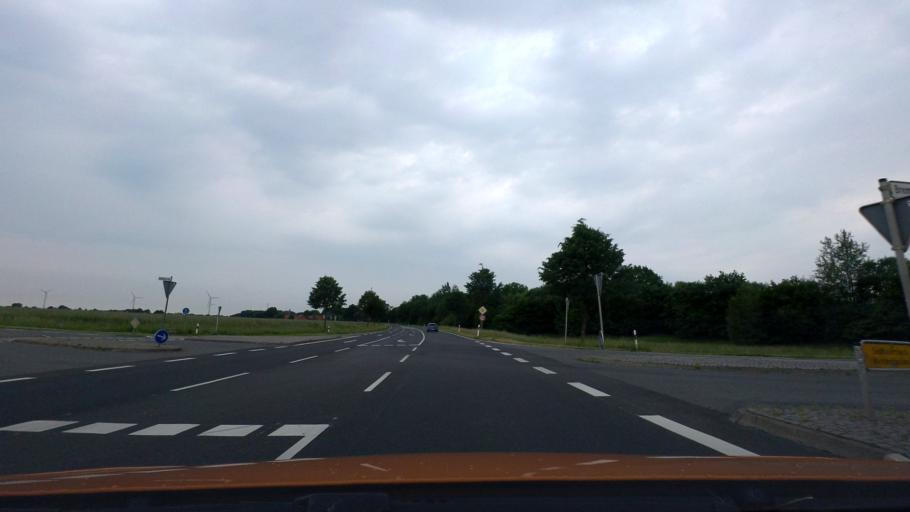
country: DE
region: Lower Saxony
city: Wietzen
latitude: 52.6769
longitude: 9.1061
